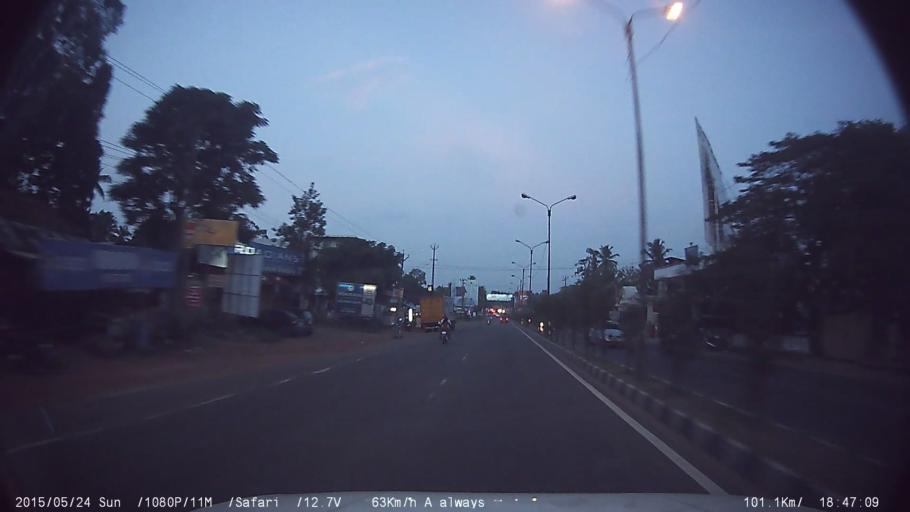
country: IN
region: Kerala
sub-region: Ernakulam
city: Aluva
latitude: 10.1303
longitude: 76.3467
